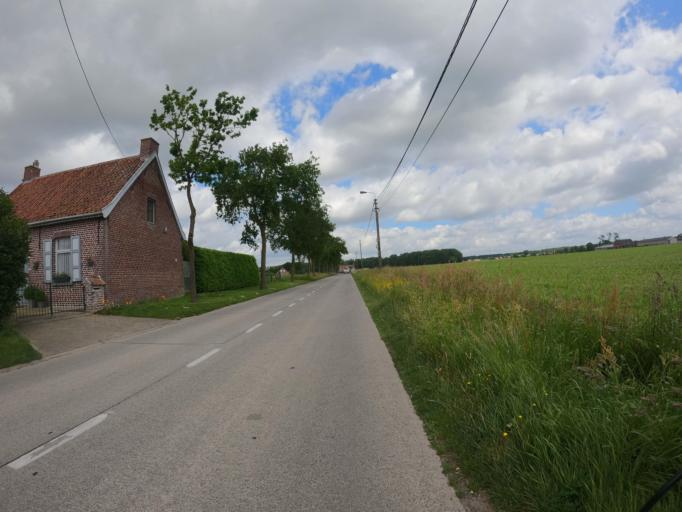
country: BE
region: Flanders
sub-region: Provincie West-Vlaanderen
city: Ruiselede
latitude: 51.0614
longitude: 3.3756
